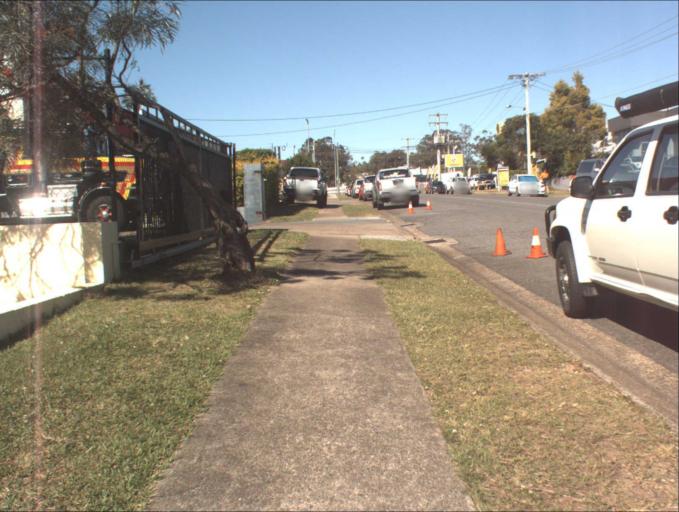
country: AU
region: Queensland
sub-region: Logan
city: Springwood
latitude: -27.6305
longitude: 153.1288
